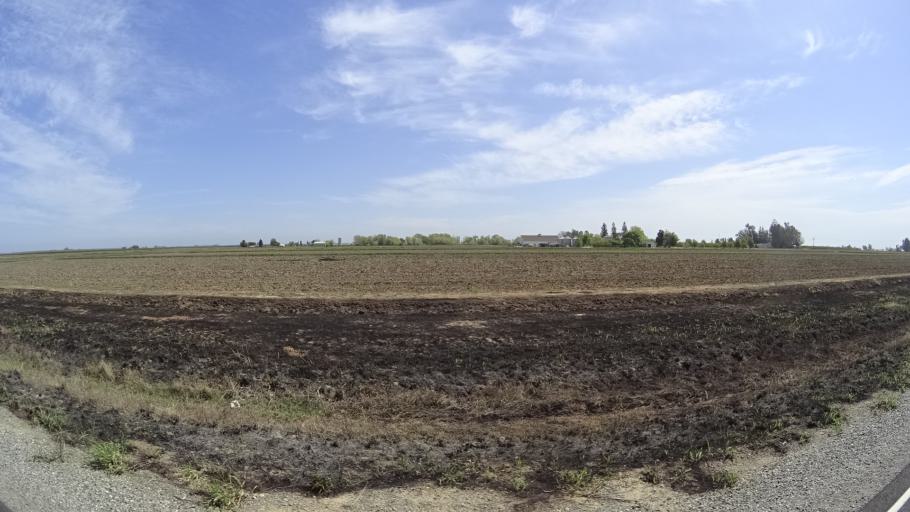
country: US
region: California
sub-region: Glenn County
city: Hamilton City
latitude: 39.6045
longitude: -122.0656
